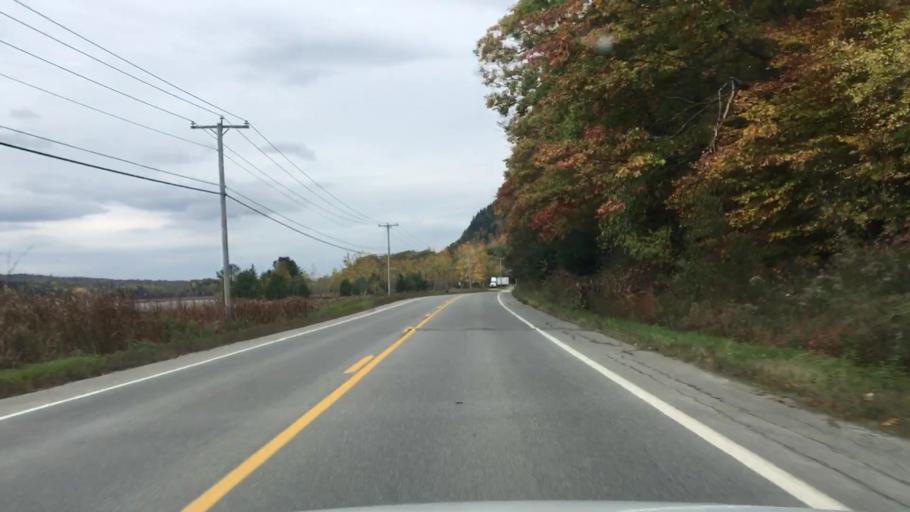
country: US
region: Maine
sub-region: Waldo County
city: Frankfort
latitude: 44.5940
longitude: -68.8655
